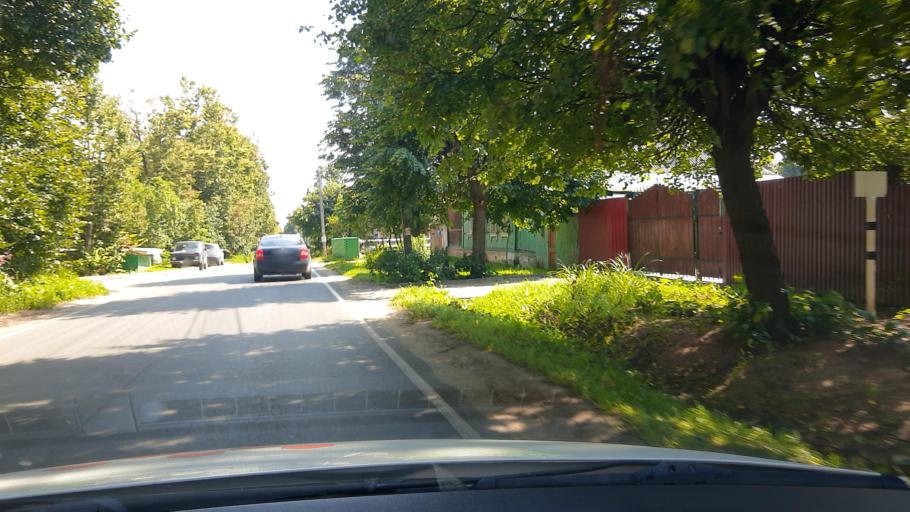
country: RU
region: Moskovskaya
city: Bronnitsy
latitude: 55.4226
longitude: 38.2636
